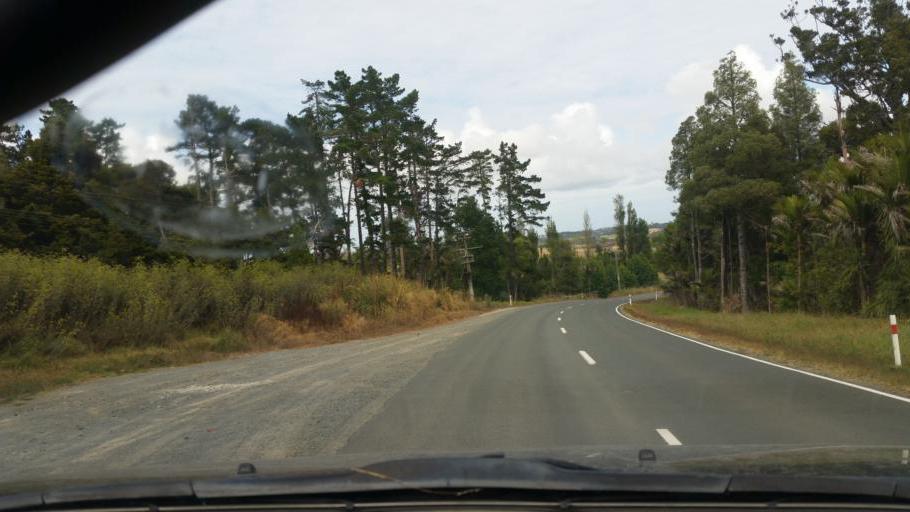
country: NZ
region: Northland
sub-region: Kaipara District
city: Dargaville
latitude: -35.9499
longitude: 173.9017
